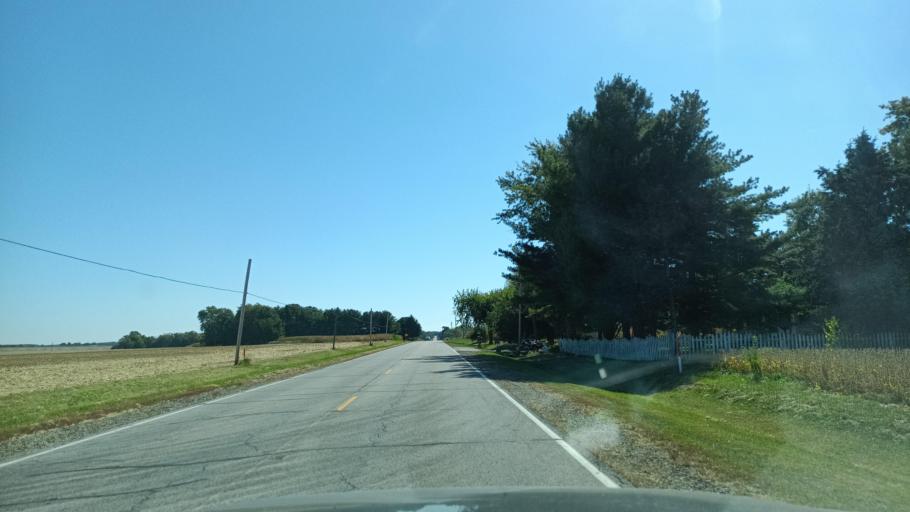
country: US
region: Illinois
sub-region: Peoria County
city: Elmwood
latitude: 40.8521
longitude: -89.9204
